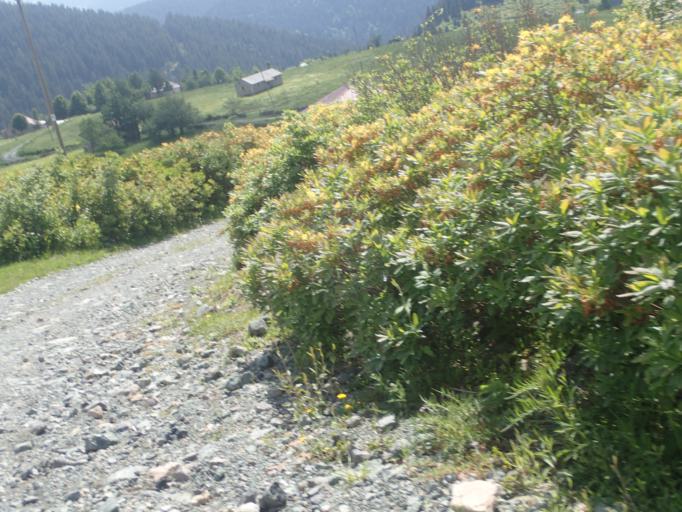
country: TR
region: Ordu
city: Kabaduz
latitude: 40.6923
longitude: 37.9510
